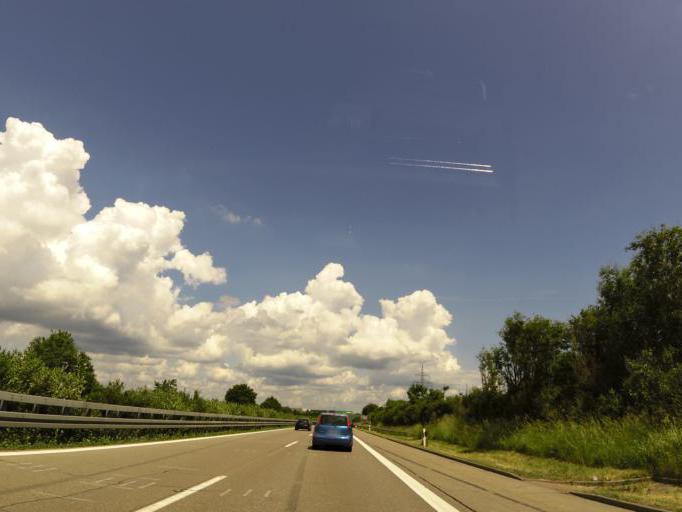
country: DE
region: Baden-Wuerttemberg
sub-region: Regierungsbezirk Stuttgart
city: Herbrechtingen
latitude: 48.5994
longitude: 10.1922
